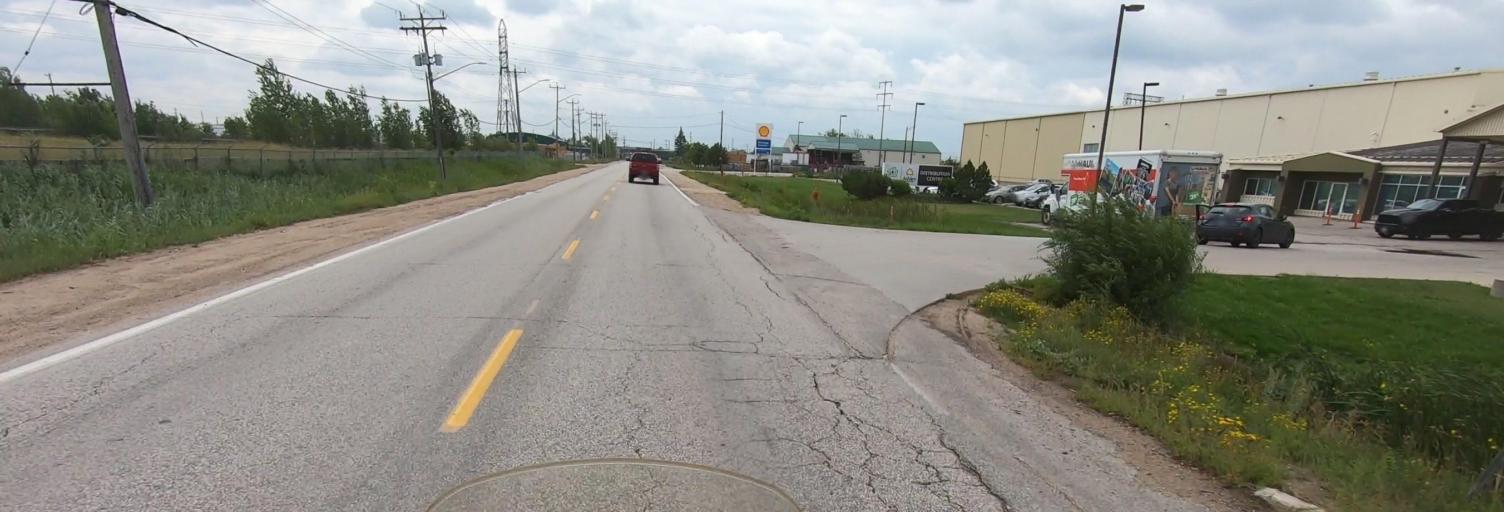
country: CA
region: Manitoba
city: Winnipeg
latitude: 49.8902
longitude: -97.0790
